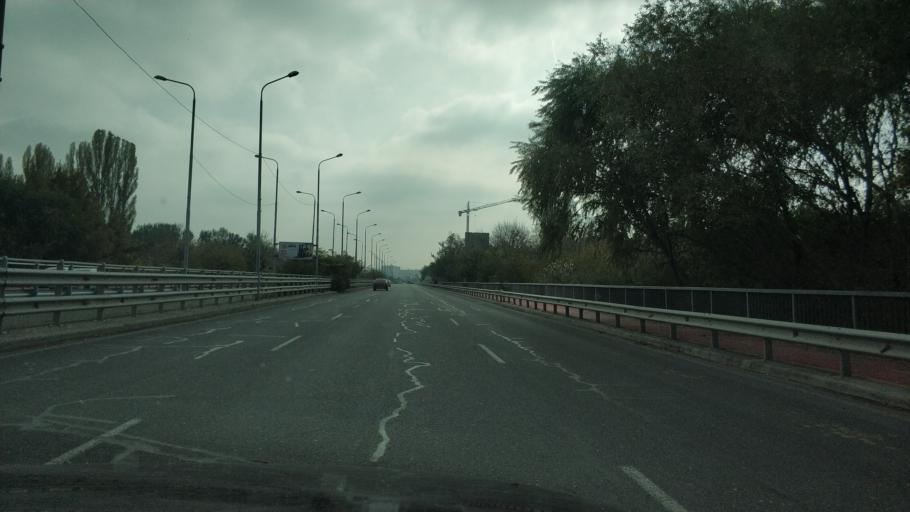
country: BG
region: Plovdiv
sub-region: Obshtina Plovdiv
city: Plovdiv
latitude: 42.1570
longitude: 24.7652
